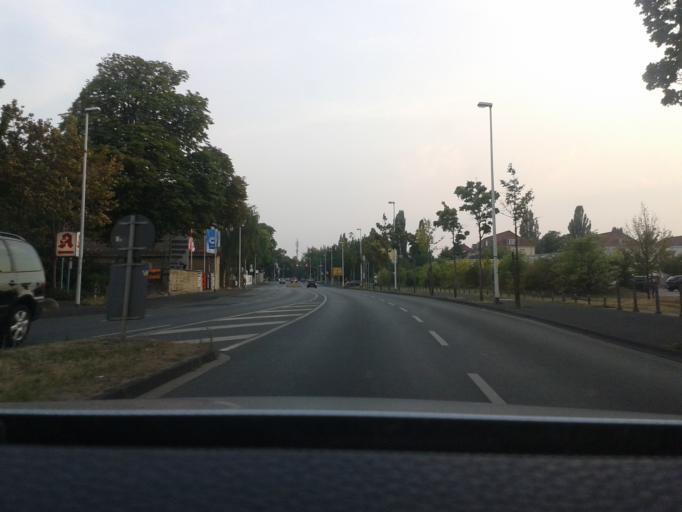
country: DE
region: Saxony
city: Albertstadt
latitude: 51.0295
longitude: 13.8022
